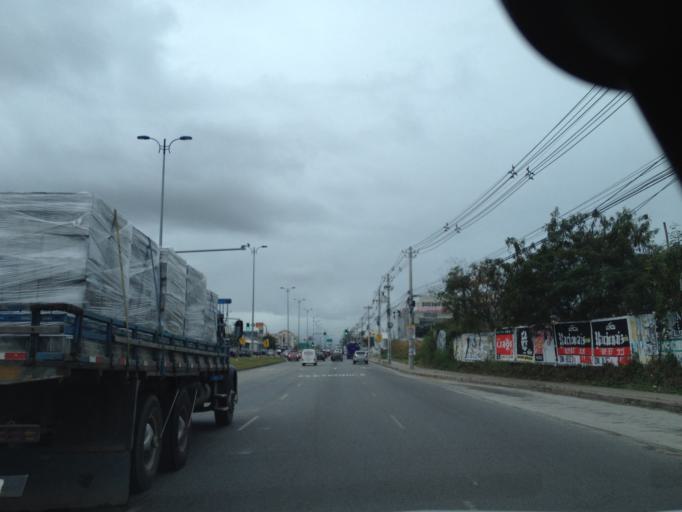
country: BR
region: Rio de Janeiro
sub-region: Nilopolis
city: Nilopolis
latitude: -23.0193
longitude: -43.4848
